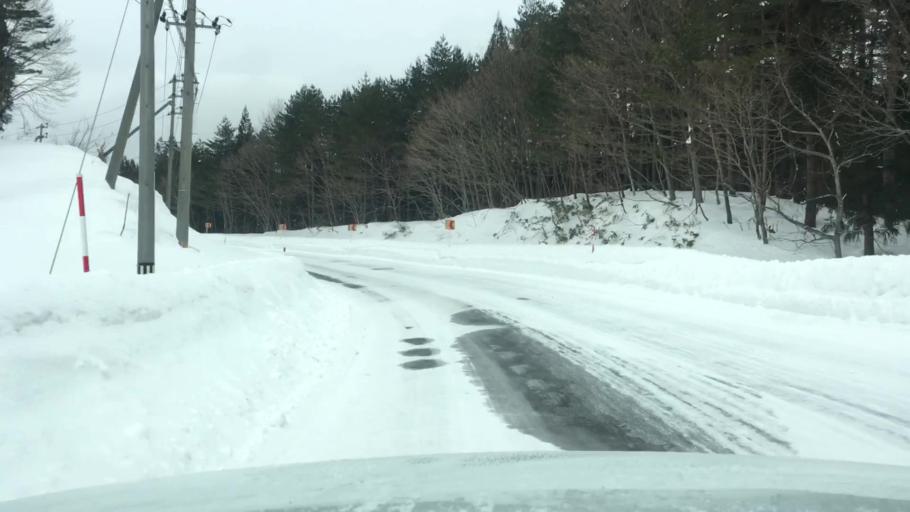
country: JP
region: Akita
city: Hanawa
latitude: 39.9945
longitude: 140.9951
